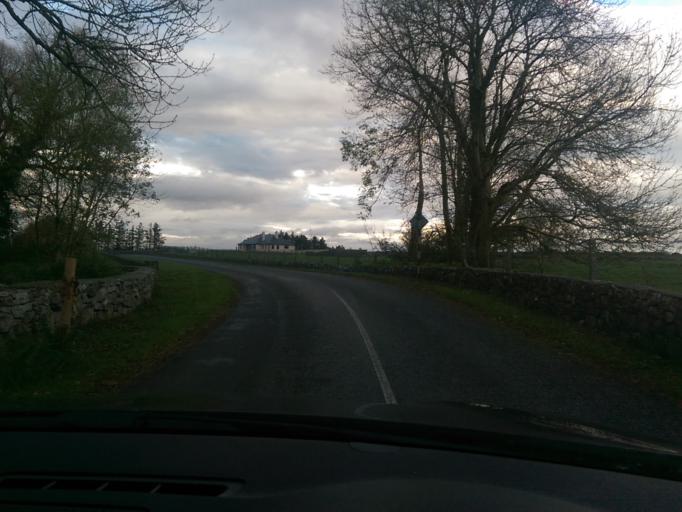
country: IE
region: Connaught
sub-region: County Galway
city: Athenry
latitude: 53.4220
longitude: -8.5725
